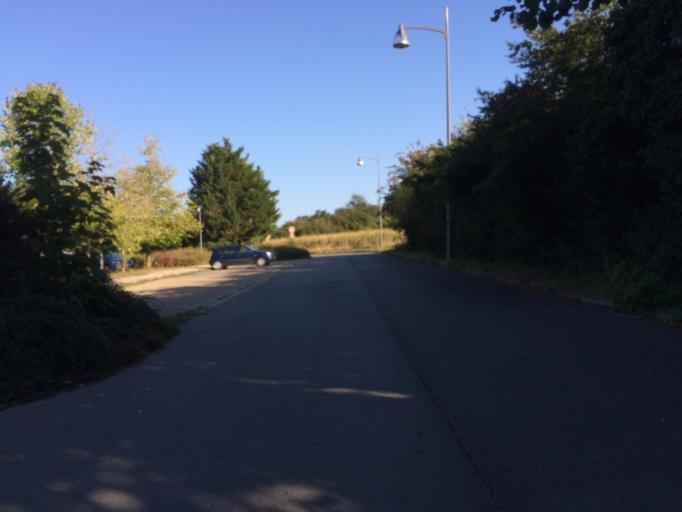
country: FR
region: Ile-de-France
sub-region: Departement de l'Essonne
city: Longjumeau
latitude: 48.6892
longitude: 2.3059
